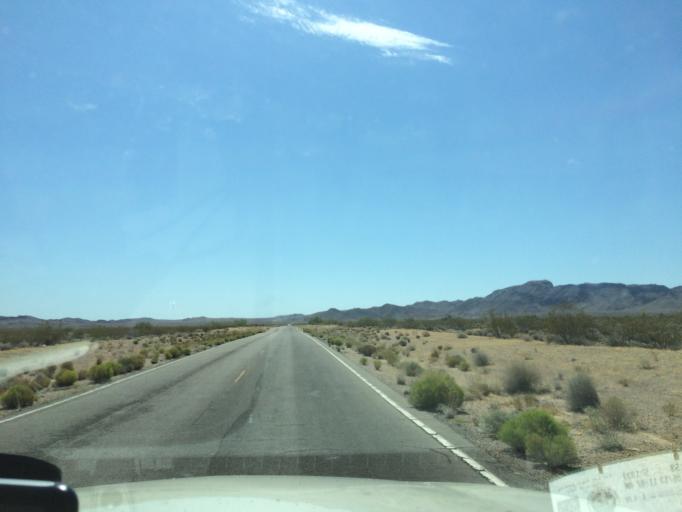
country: US
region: Nevada
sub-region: Clark County
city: Moapa Town
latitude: 36.4554
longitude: -114.7150
